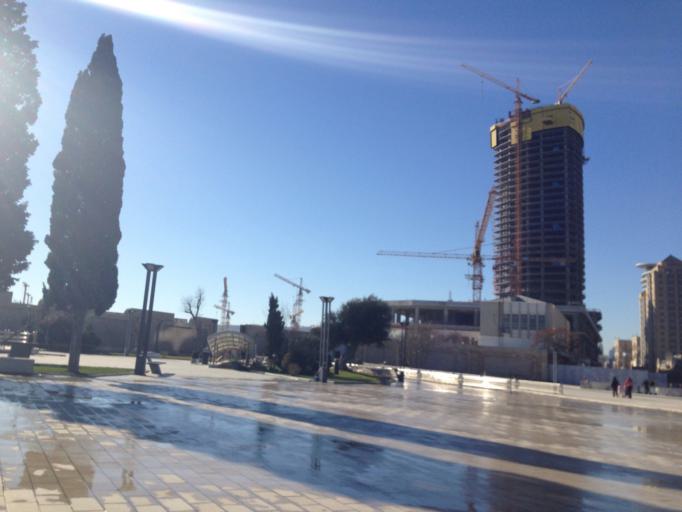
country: AZ
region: Baki
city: Baku
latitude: 40.3749
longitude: 49.8630
